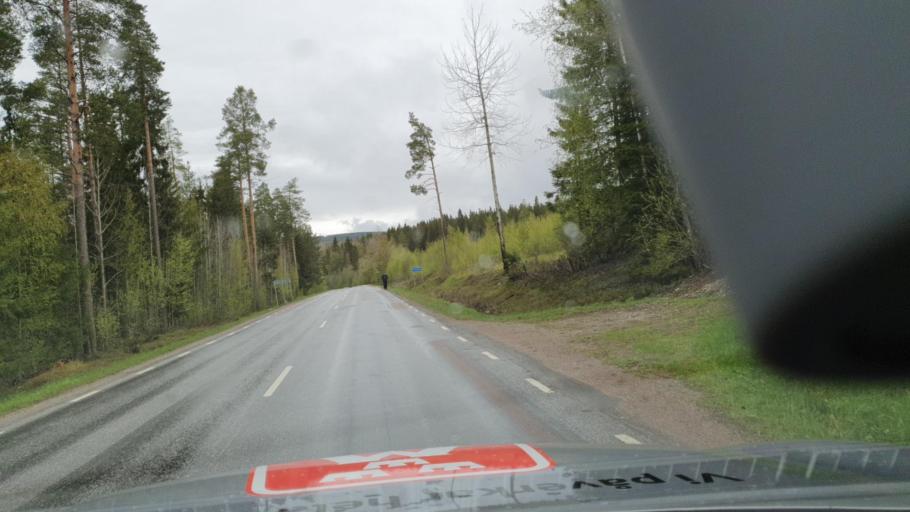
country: SE
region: Vaesternorrland
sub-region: OErnskoeldsviks Kommun
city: Bjasta
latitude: 63.3417
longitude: 18.5355
